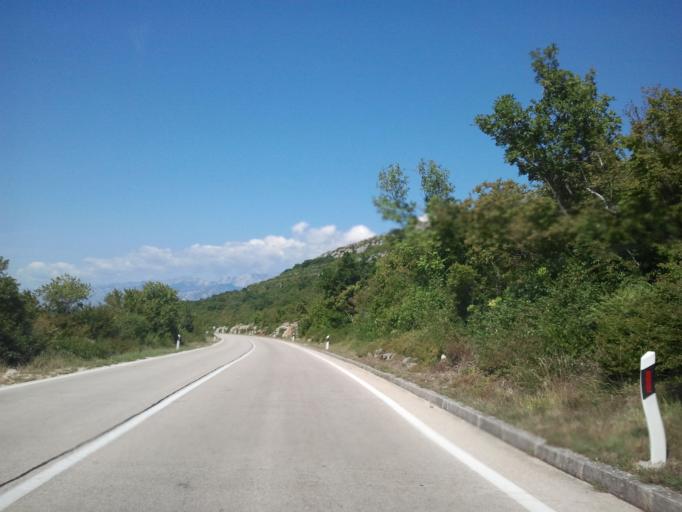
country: HR
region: Zadarska
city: Krusevo
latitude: 44.1682
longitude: 15.6253
